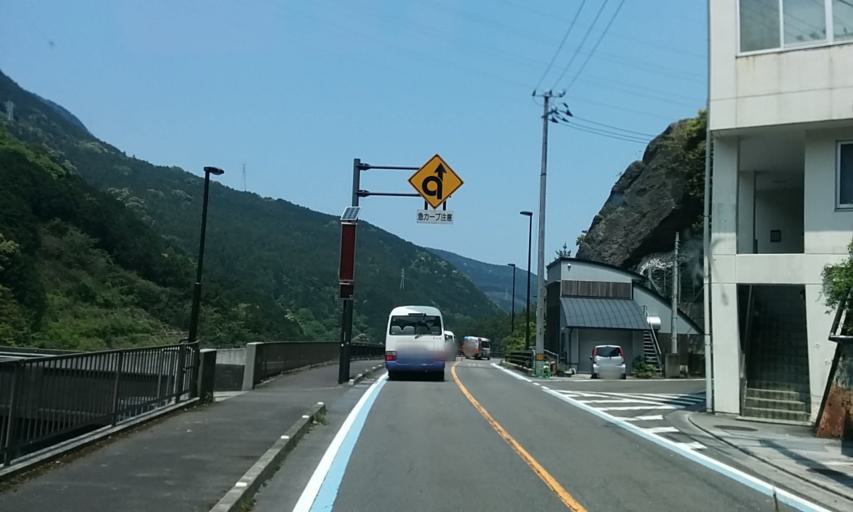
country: JP
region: Ehime
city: Niihama
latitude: 33.8937
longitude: 133.3104
